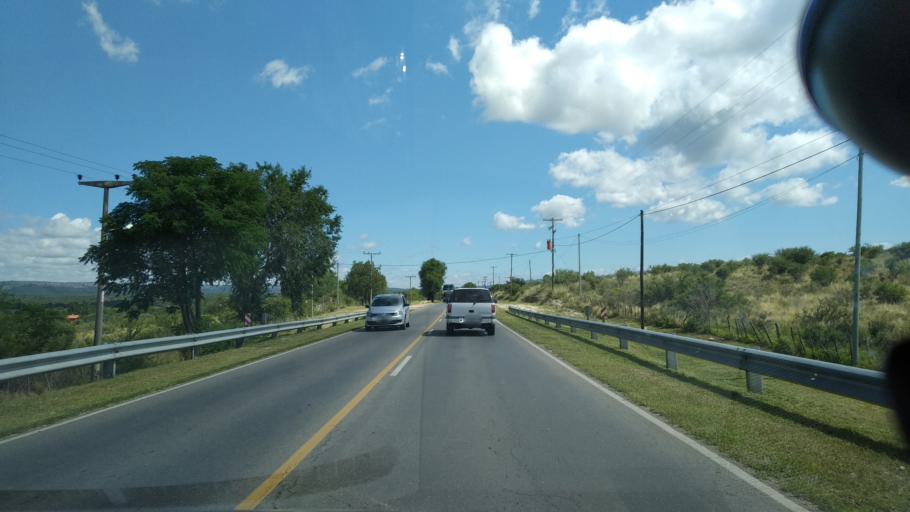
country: AR
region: Cordoba
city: Mina Clavero
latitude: -31.7826
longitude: -64.9992
